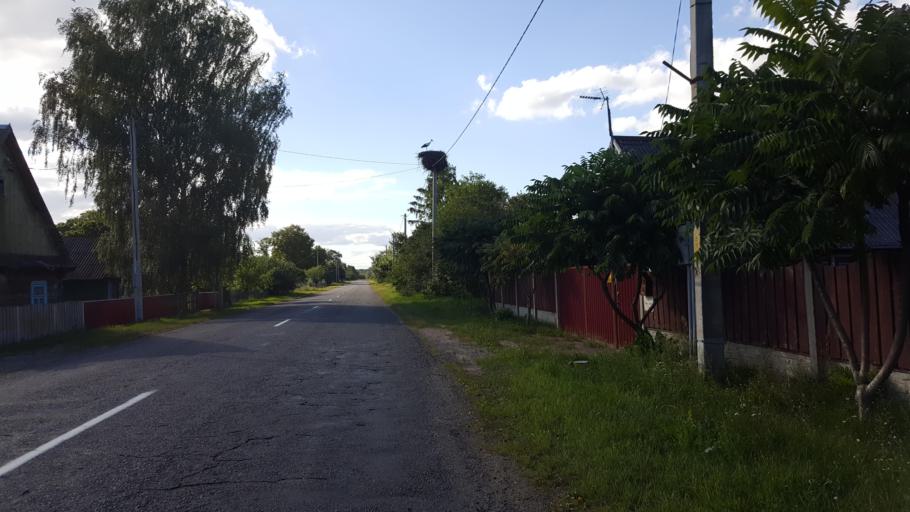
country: BY
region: Brest
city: Zhabinka
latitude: 52.3640
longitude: 24.1501
